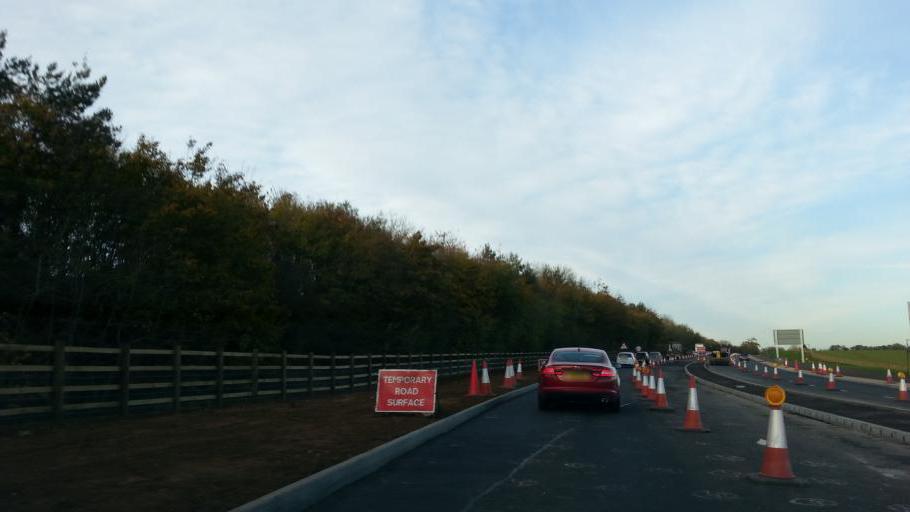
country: GB
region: England
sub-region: Northamptonshire
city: Northampton
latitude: 52.2907
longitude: -0.8366
